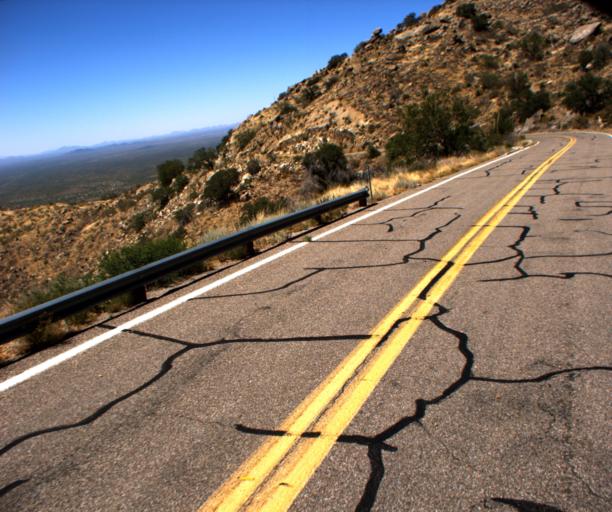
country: US
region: Arizona
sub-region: Pima County
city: Sells
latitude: 31.9758
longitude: -111.6039
